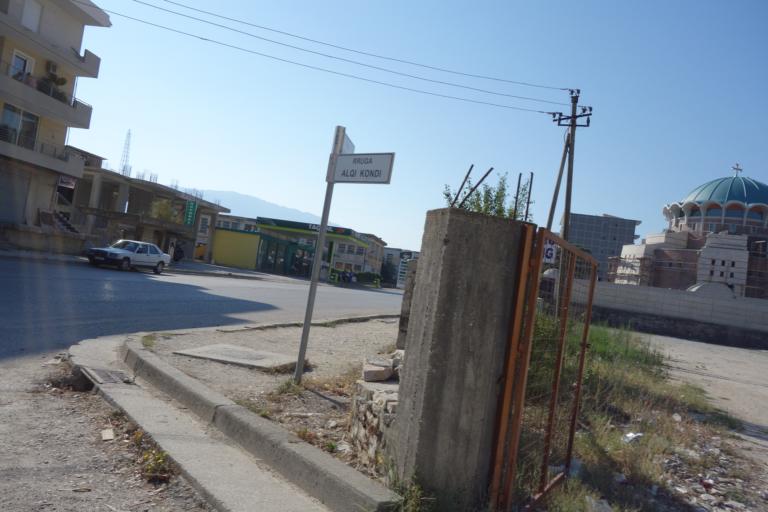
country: AL
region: Gjirokaster
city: Gjirokaster
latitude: 40.0812
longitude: 20.1472
